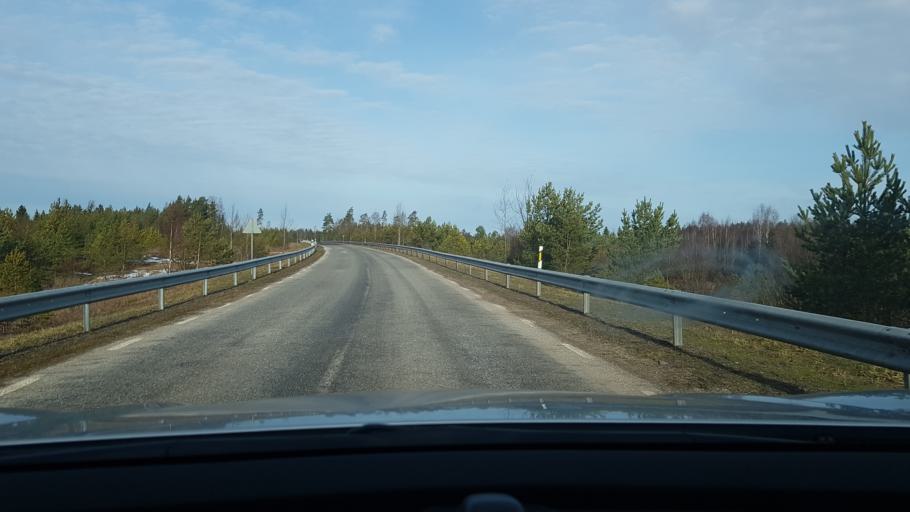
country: EE
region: Saare
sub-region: Kuressaare linn
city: Kuressaare
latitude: 58.4584
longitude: 22.7071
